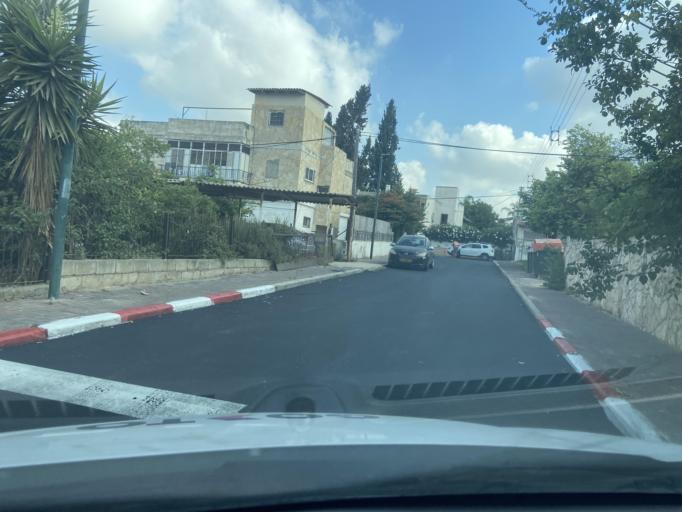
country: IL
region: Central District
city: Yehud
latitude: 32.0377
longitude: 34.8876
